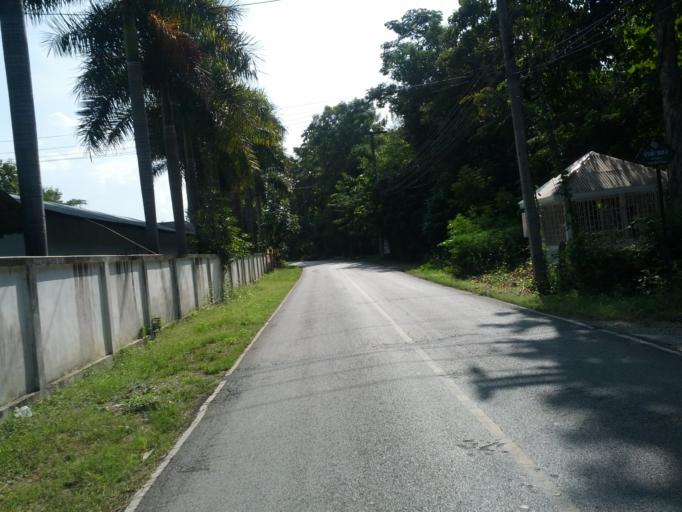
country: TH
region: Chiang Mai
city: San Kamphaeng
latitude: 18.7630
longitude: 99.1159
